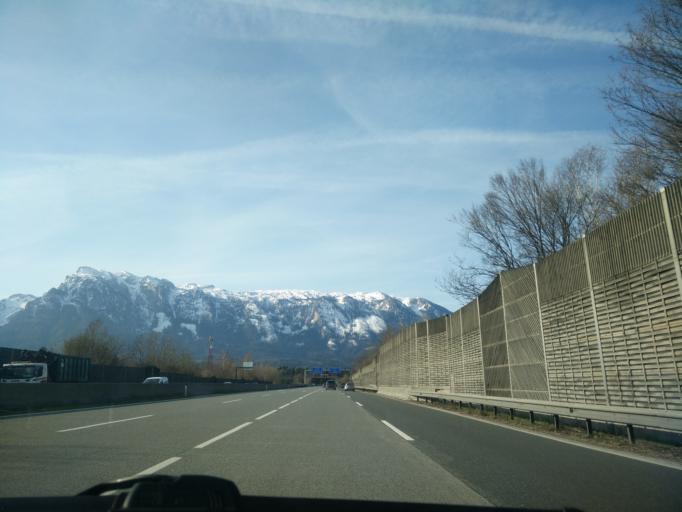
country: DE
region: Bavaria
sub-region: Upper Bavaria
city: Ainring
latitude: 47.7823
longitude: 12.9805
